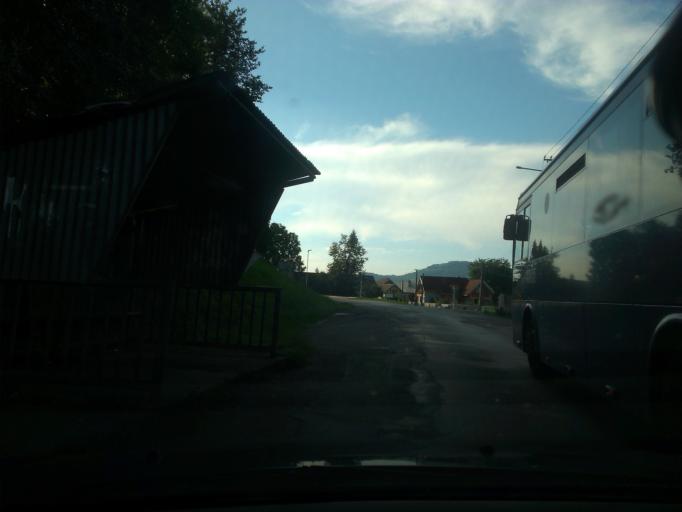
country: SK
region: Zilinsky
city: Krasnany
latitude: 49.1855
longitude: 18.8610
